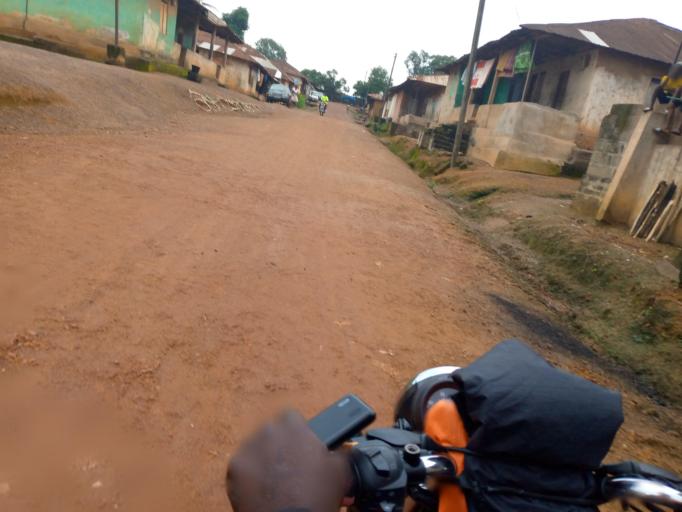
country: SL
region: Eastern Province
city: Kenema
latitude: 7.8682
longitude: -11.1880
